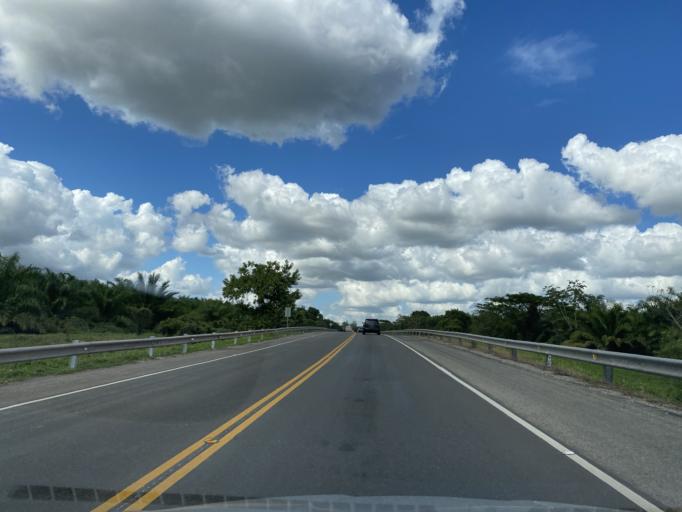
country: DO
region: Monte Plata
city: Monte Plata
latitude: 18.7137
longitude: -69.7566
